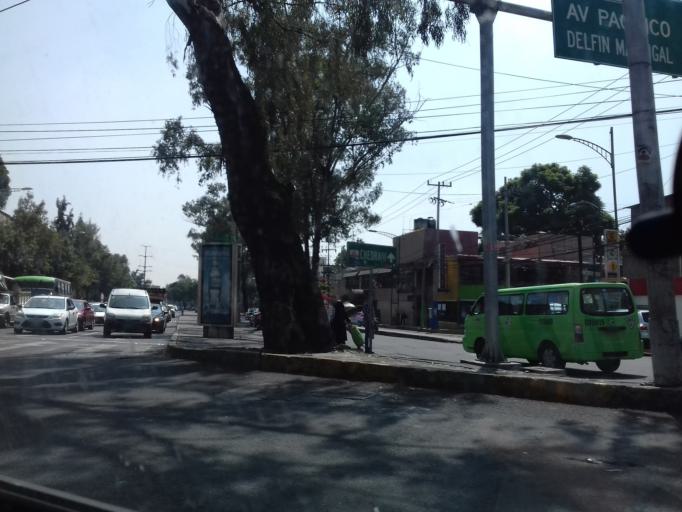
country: MX
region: Mexico City
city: Coyoacan
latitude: 19.3374
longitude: -99.1838
